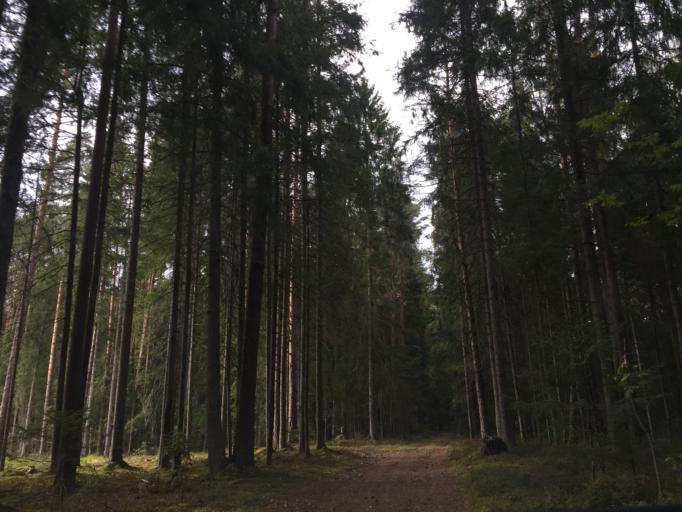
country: LV
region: Baldone
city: Baldone
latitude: 56.7825
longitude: 24.4433
